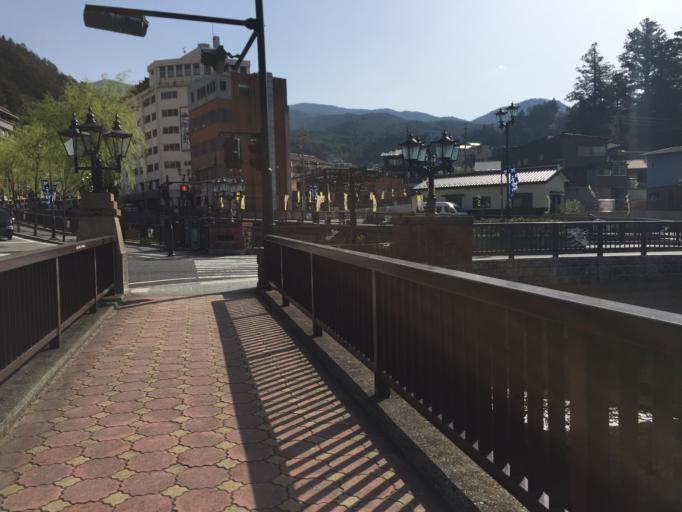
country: JP
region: Gifu
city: Gujo
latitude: 35.8076
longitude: 137.2422
